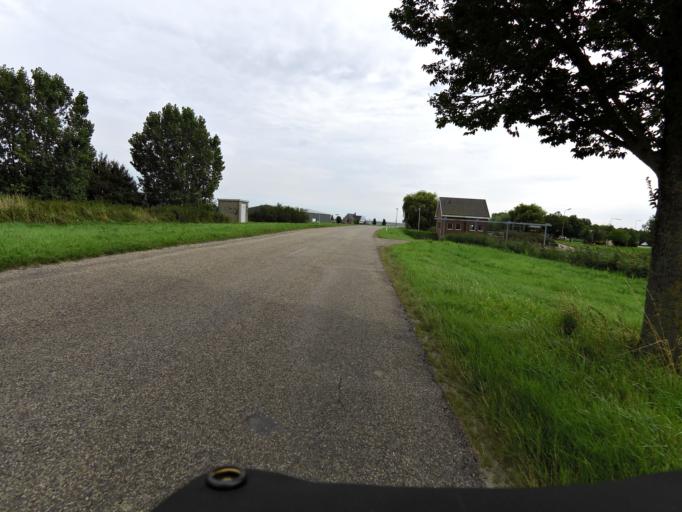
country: NL
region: South Holland
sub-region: Gemeente Goeree-Overflakkee
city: Middelharnis
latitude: 51.6943
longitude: 4.2249
